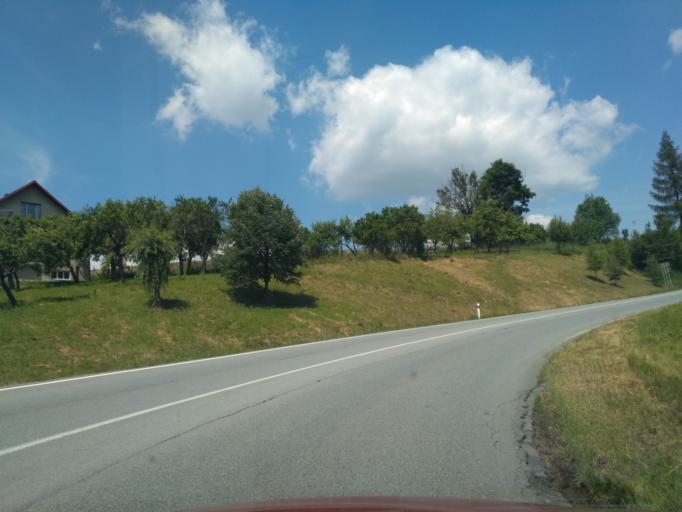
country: SK
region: Presovsky
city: Stara L'ubovna
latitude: 49.2669
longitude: 20.7716
